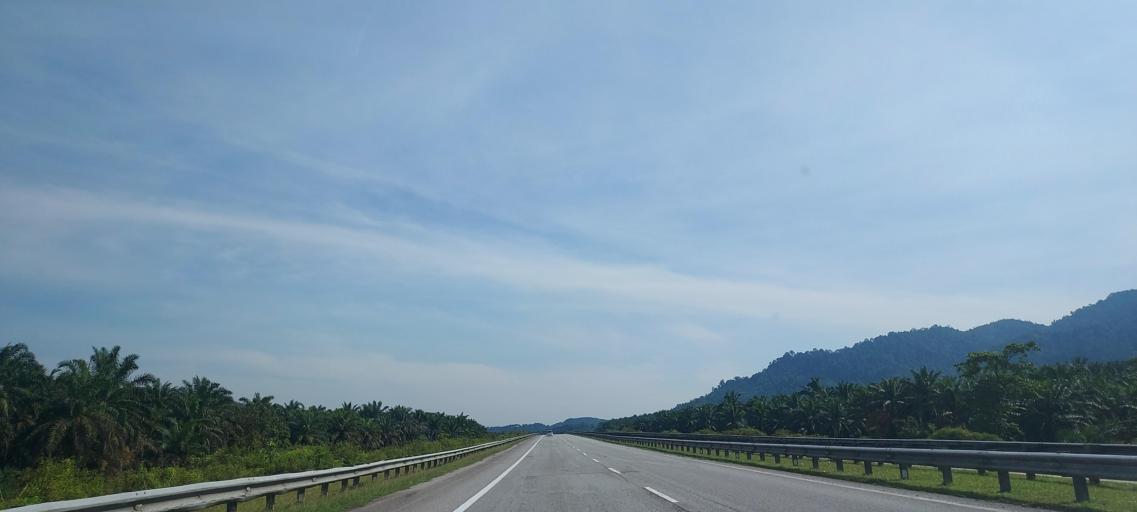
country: MY
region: Terengganu
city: Marang
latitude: 4.9707
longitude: 103.0806
